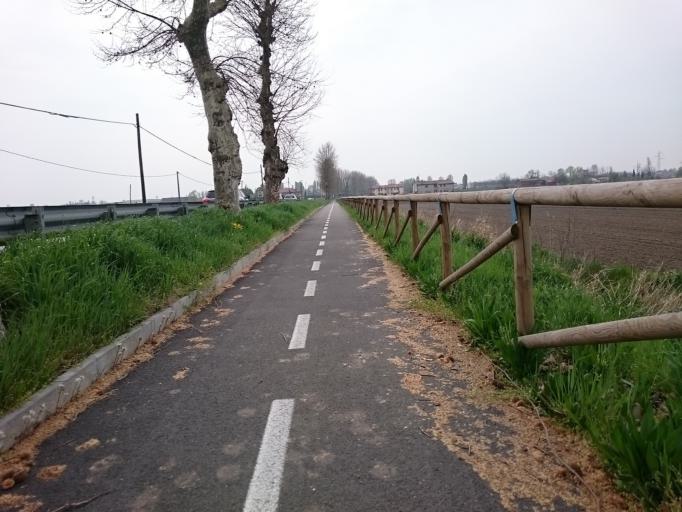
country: IT
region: Veneto
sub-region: Provincia di Padova
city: Anguillara Veneta
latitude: 45.1559
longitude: 11.8766
